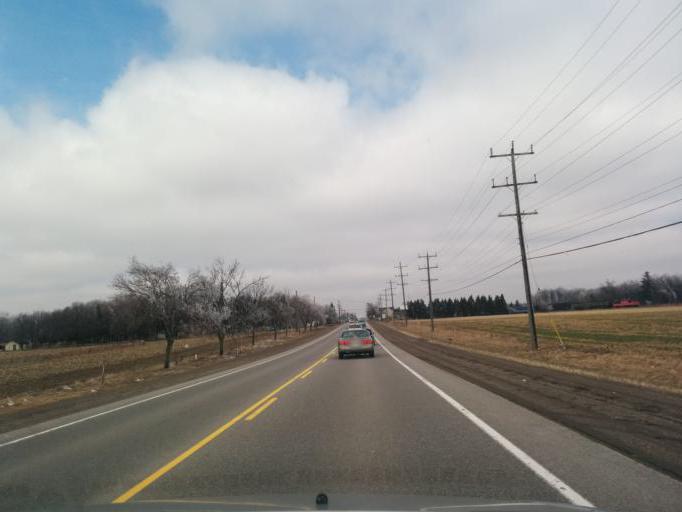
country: CA
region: Ontario
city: Waterloo
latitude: 43.5218
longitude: -80.5564
